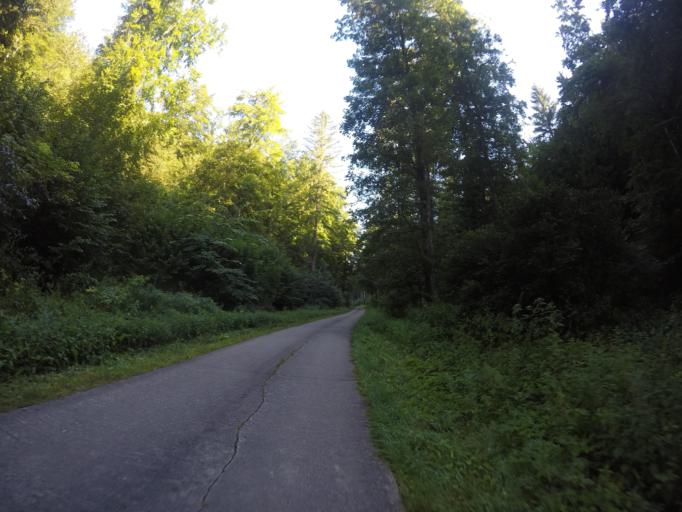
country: DE
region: Baden-Wuerttemberg
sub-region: Tuebingen Region
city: Schelklingen
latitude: 48.3850
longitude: 9.7332
